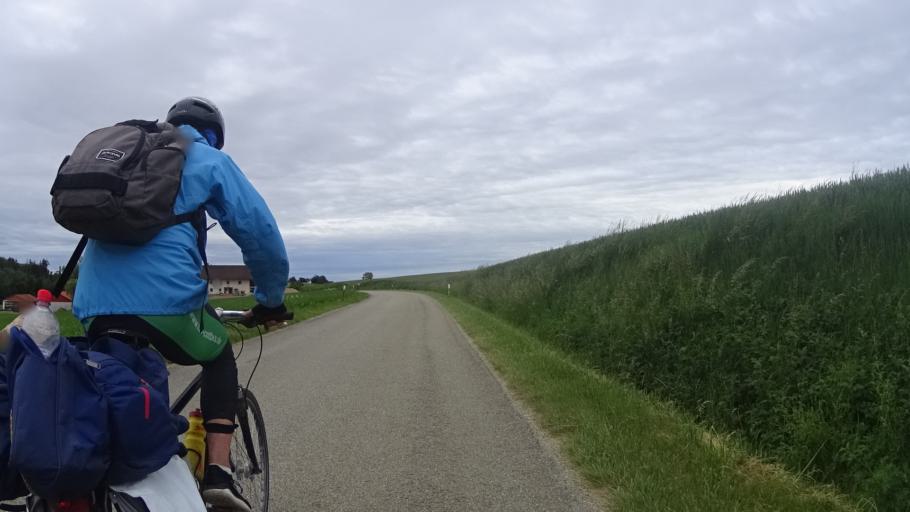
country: DE
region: Bavaria
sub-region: Lower Bavaria
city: Wurmsham
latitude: 48.3890
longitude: 12.3264
